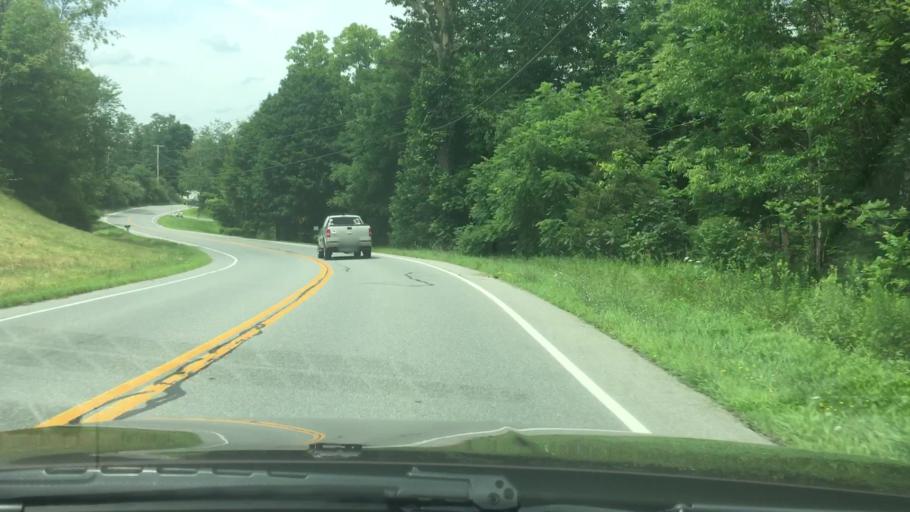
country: US
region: New York
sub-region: Dutchess County
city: Hillside Lake
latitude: 41.6514
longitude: -73.7480
